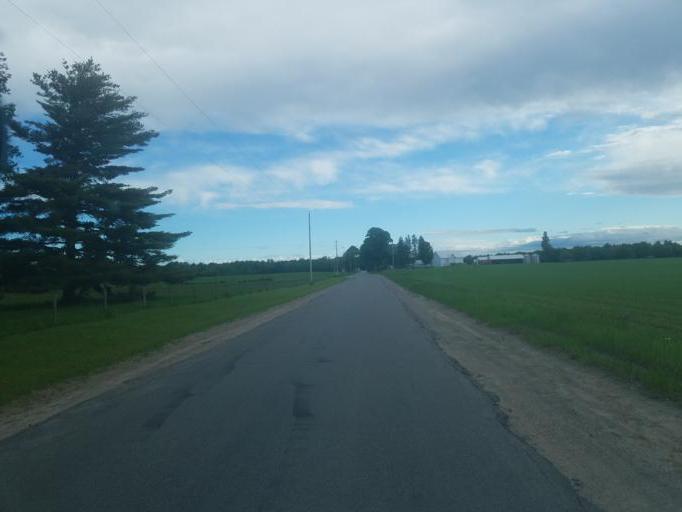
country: US
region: New York
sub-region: Herkimer County
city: Herkimer
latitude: 43.2609
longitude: -74.9817
